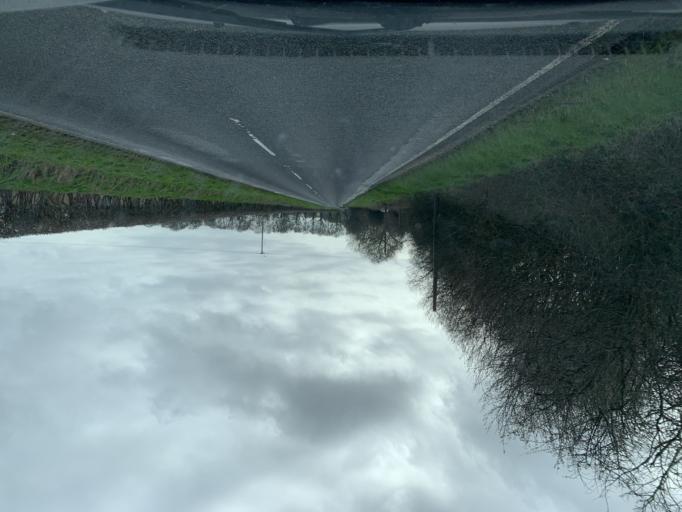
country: GB
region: England
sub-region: Wiltshire
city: Downton
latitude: 50.9695
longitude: -1.7677
